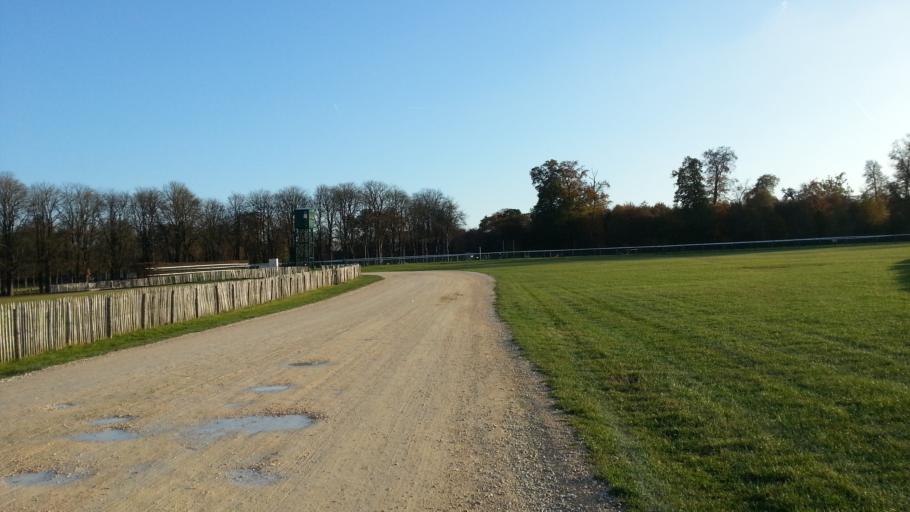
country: FR
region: Picardie
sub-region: Departement de l'Oise
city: Chantilly
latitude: 49.1922
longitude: 2.4827
